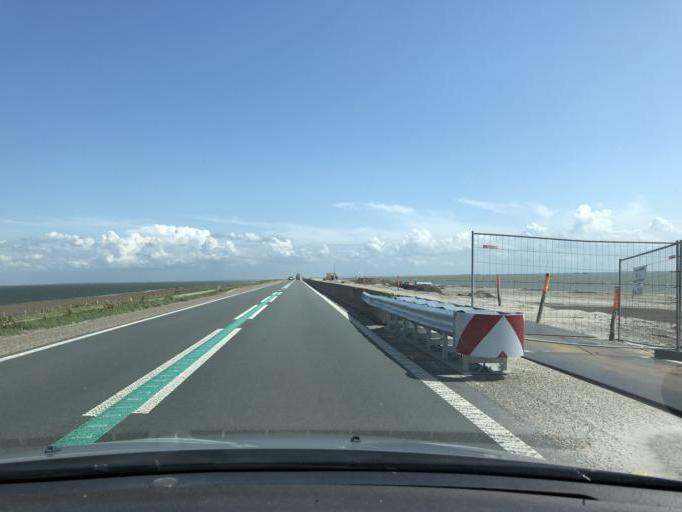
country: NL
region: North Holland
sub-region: Gemeente Enkhuizen
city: Enkhuizen
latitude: 52.6866
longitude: 5.3197
